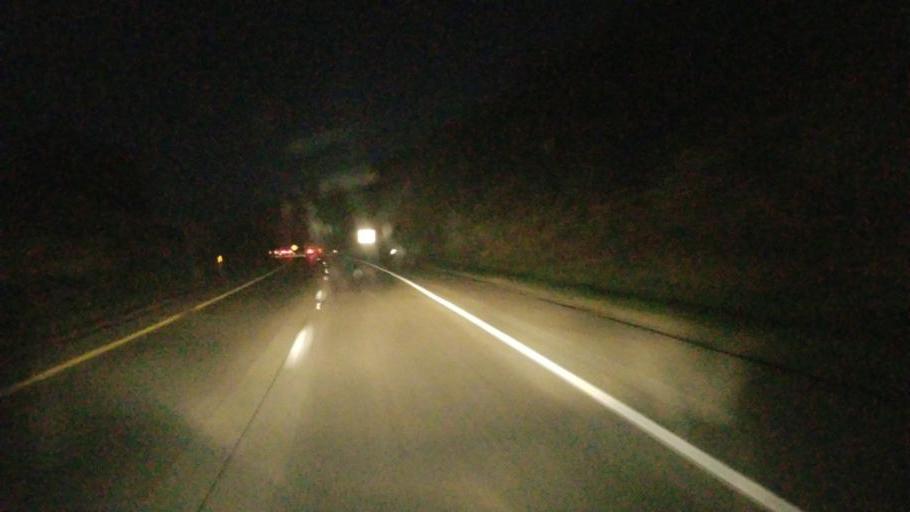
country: US
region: Pennsylvania
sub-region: Greene County
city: Waynesburg
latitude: 40.0038
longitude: -80.1883
